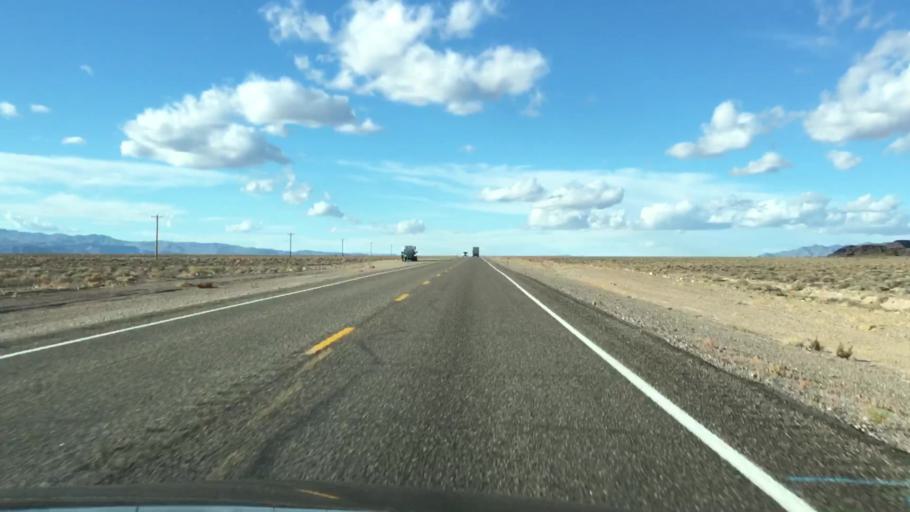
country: US
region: Nevada
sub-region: Nye County
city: Beatty
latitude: 37.1943
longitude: -116.9474
